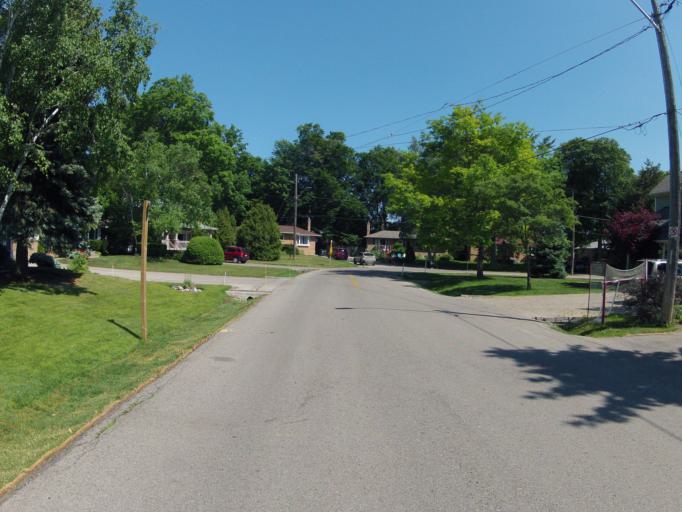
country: CA
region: Ontario
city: Mississauga
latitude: 43.5167
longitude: -79.6333
